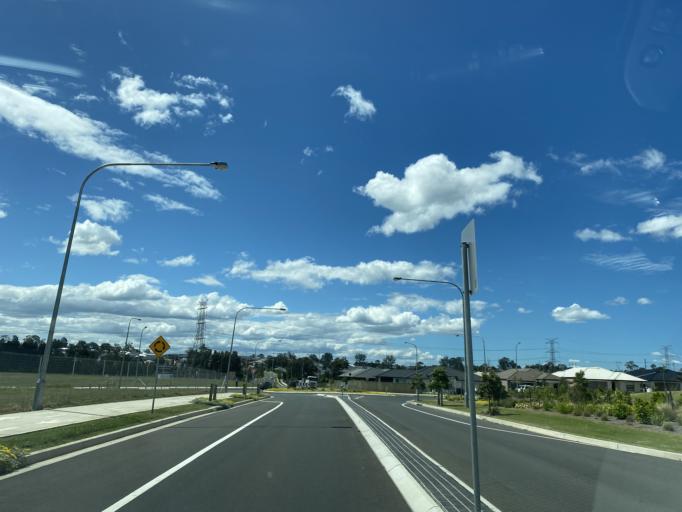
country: AU
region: New South Wales
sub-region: Camden
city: Narellan Vale
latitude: -34.0220
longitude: 150.7728
